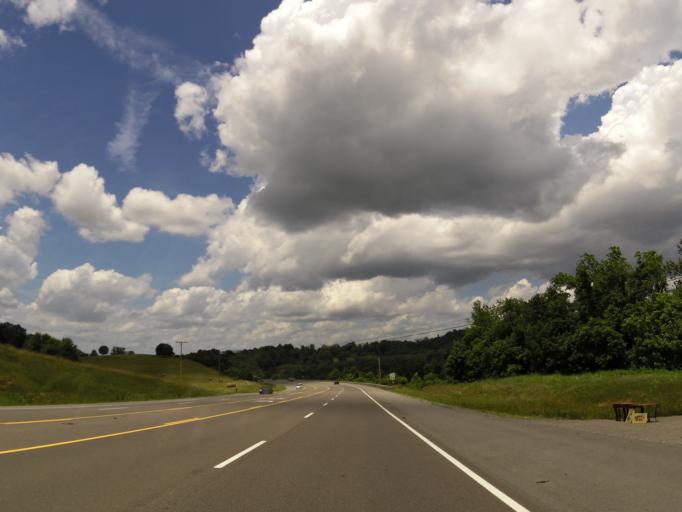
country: US
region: Tennessee
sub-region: Claiborne County
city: Tazewell
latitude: 36.4992
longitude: -83.5936
